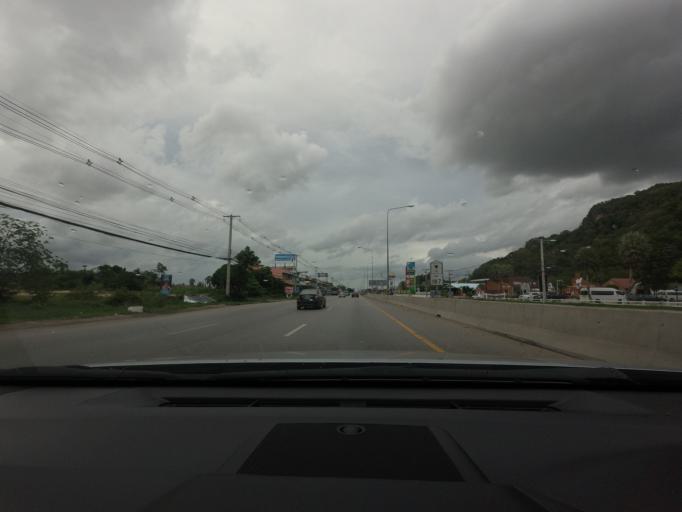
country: TH
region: Phetchaburi
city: Cha-am
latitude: 12.8159
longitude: 99.9412
